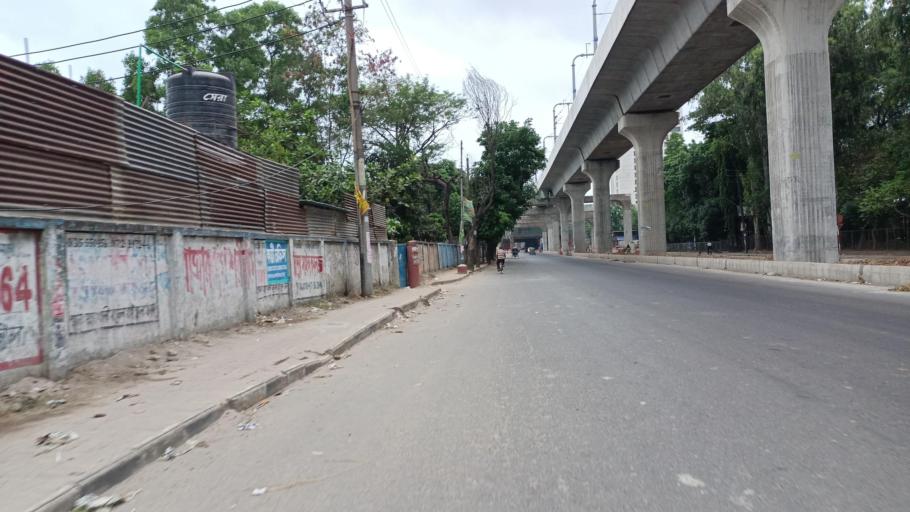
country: BD
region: Dhaka
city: Azimpur
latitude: 23.7817
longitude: 90.3792
